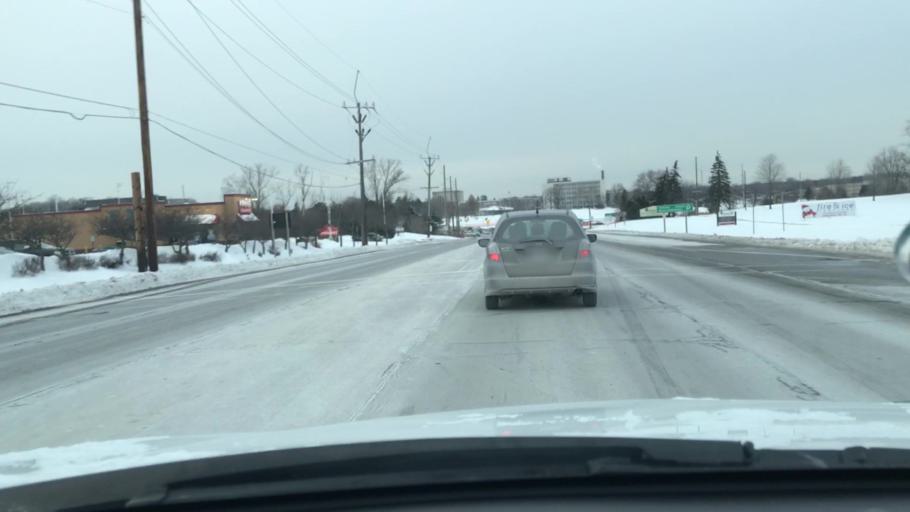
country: US
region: Michigan
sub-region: Oakland County
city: Sylvan Lake
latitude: 42.6473
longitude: -83.3262
